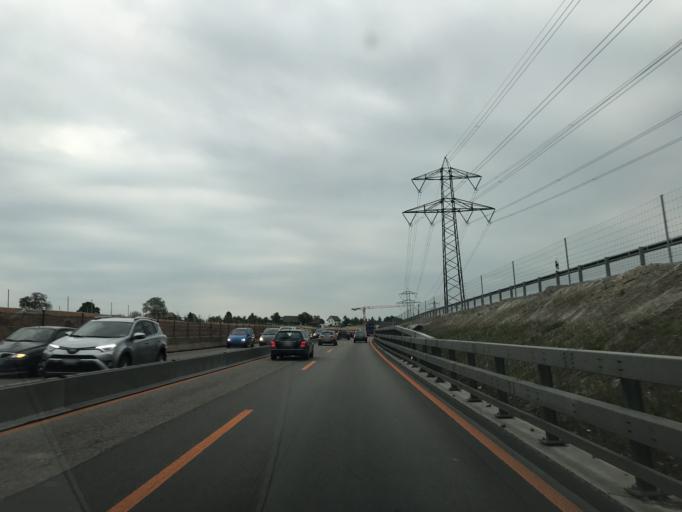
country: CH
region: Zurich
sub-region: Bezirk Zuerich
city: Zuerich (Kreis 11) / Schwandenholz
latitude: 47.4320
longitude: 8.5201
